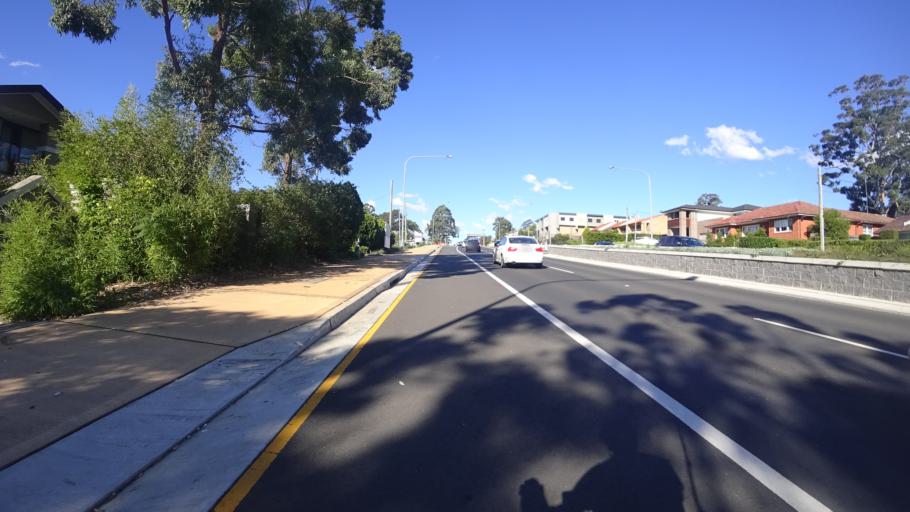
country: AU
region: New South Wales
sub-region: The Hills Shire
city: Castle Hill
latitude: -33.7311
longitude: 150.9994
